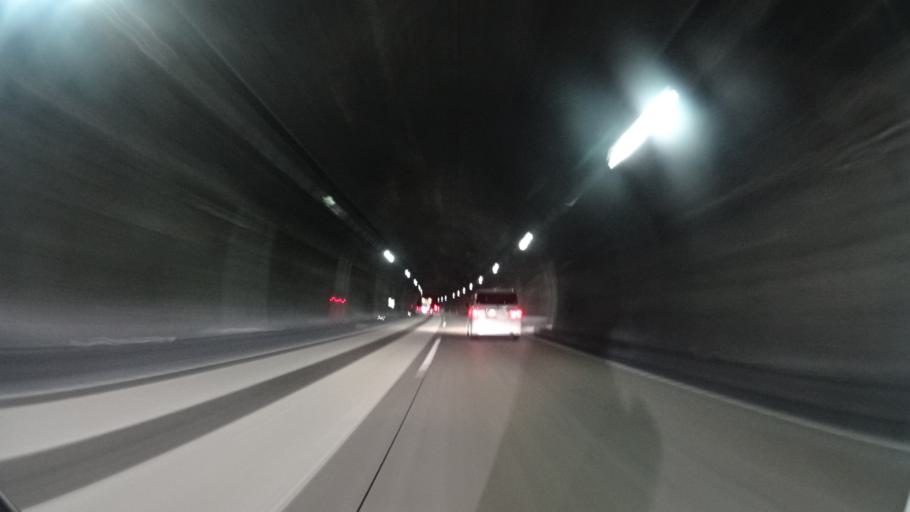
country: JP
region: Hyogo
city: Himeji
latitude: 34.8543
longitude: 134.7301
